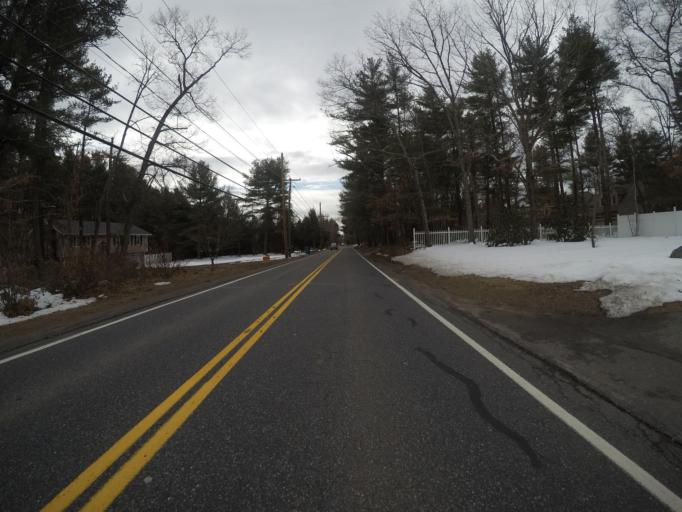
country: US
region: Massachusetts
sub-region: Bristol County
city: Easton
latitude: 42.0596
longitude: -71.1319
